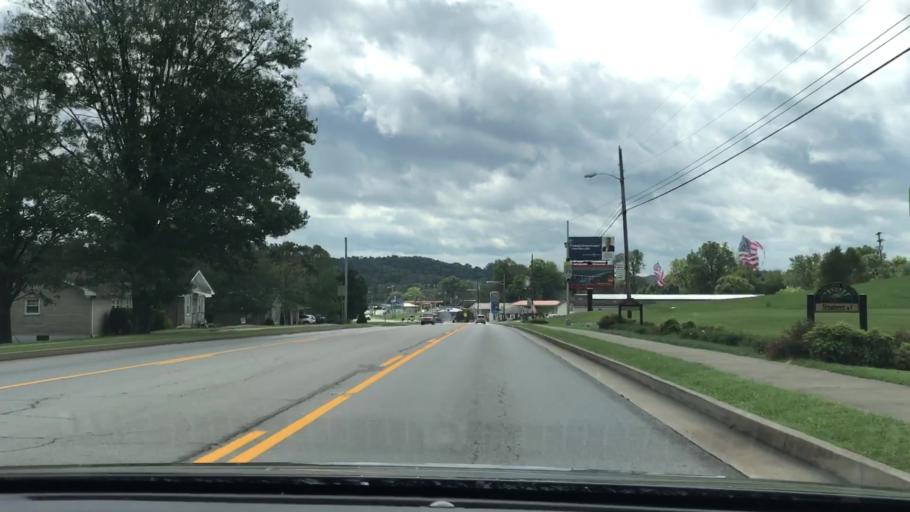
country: US
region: Kentucky
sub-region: Cumberland County
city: Burkesville
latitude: 36.7959
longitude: -85.3717
